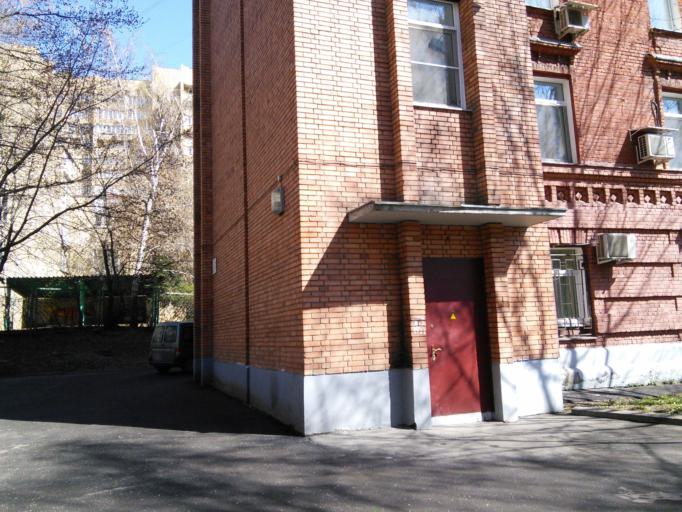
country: RU
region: Moscow
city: Taganskiy
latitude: 55.7359
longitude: 37.6528
